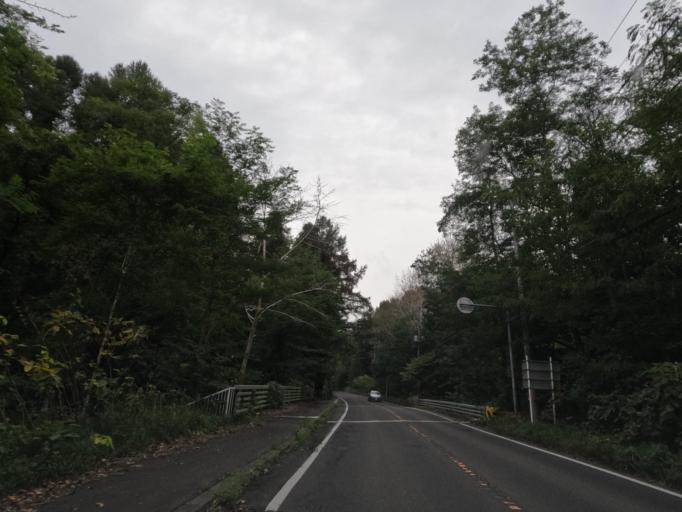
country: JP
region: Hokkaido
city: Date
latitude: 42.5476
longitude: 140.8576
